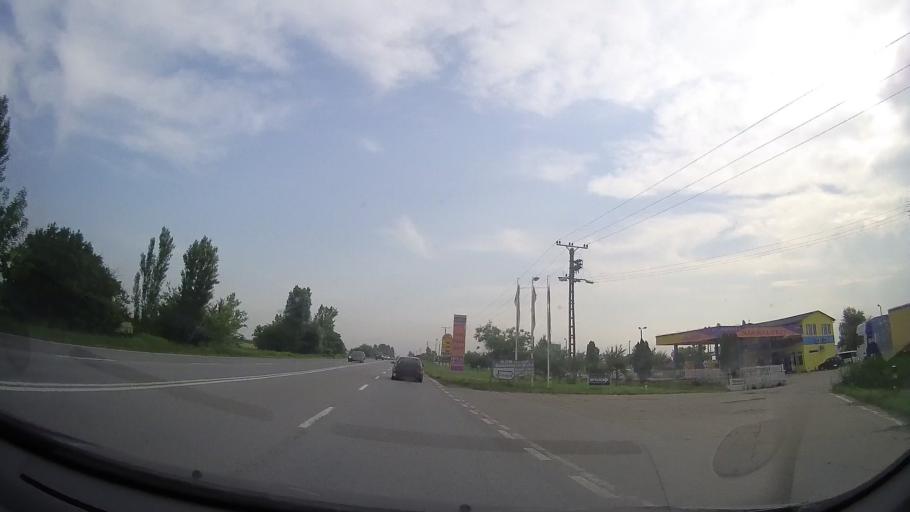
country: RO
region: Timis
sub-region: Comuna Sag
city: Sag
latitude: 45.6871
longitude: 21.1711
